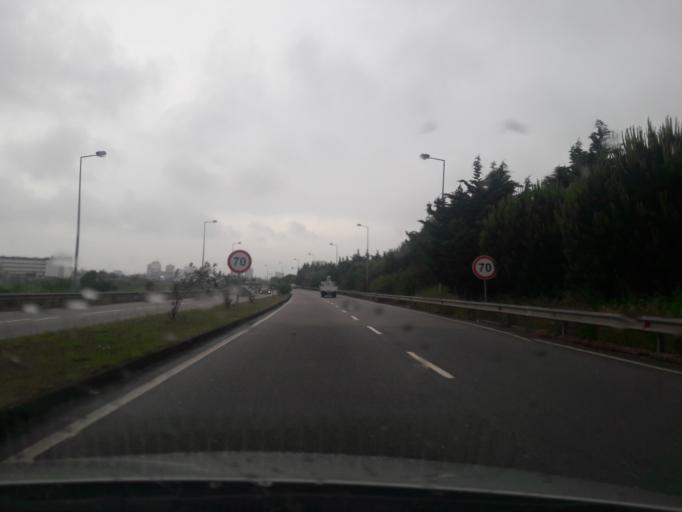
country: PT
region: Porto
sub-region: Povoa de Varzim
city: Pedroso
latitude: 41.3976
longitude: -8.7520
